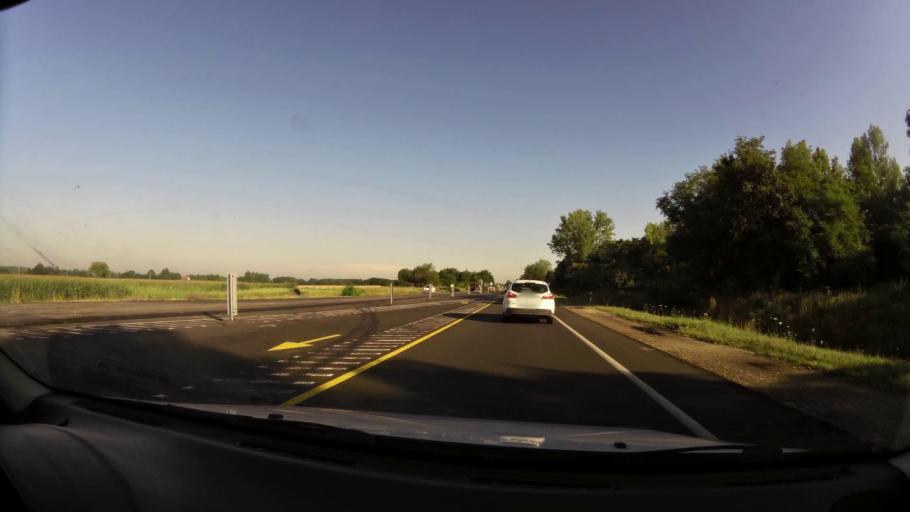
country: HU
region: Pest
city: Cegledbercel
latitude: 47.2439
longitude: 19.6539
